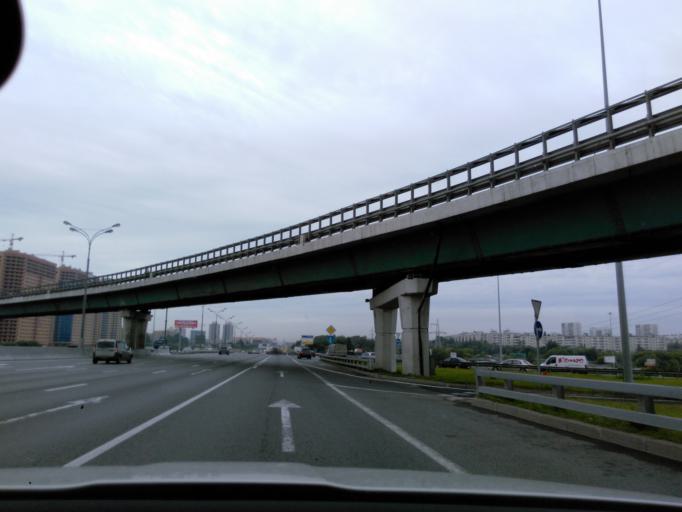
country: RU
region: Moscow
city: Ivanovskoye
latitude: 55.7784
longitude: 37.8422
